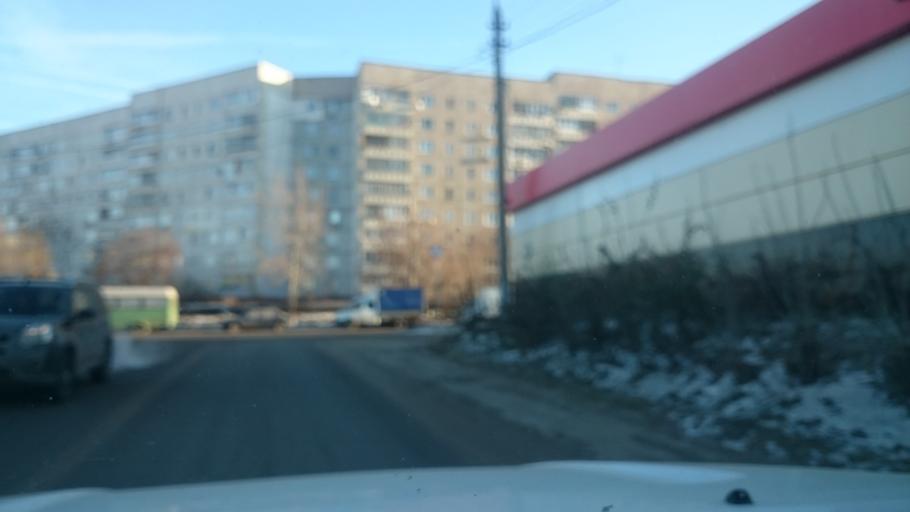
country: RU
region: Tula
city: Tula
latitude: 54.2101
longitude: 37.6842
